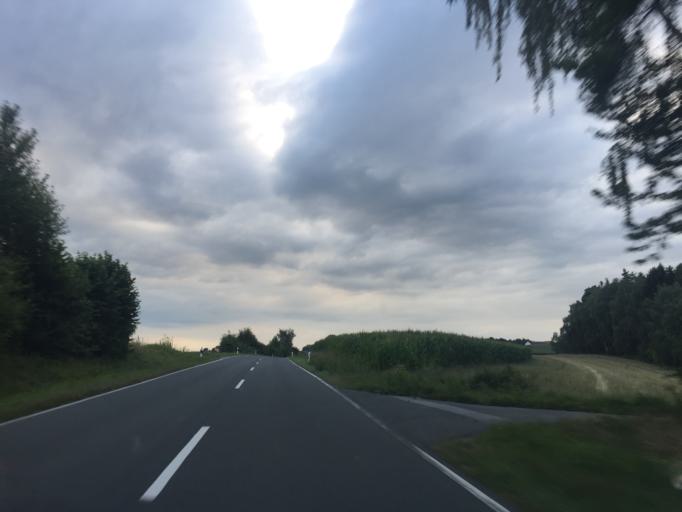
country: DE
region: Bavaria
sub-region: Upper Palatinate
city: Kirchendemenreuth
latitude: 49.7825
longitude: 12.0490
